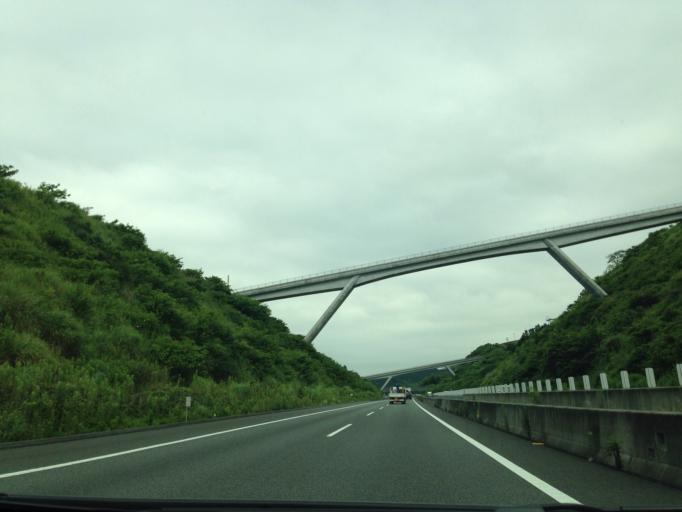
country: JP
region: Shizuoka
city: Fuji
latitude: 35.1678
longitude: 138.7517
